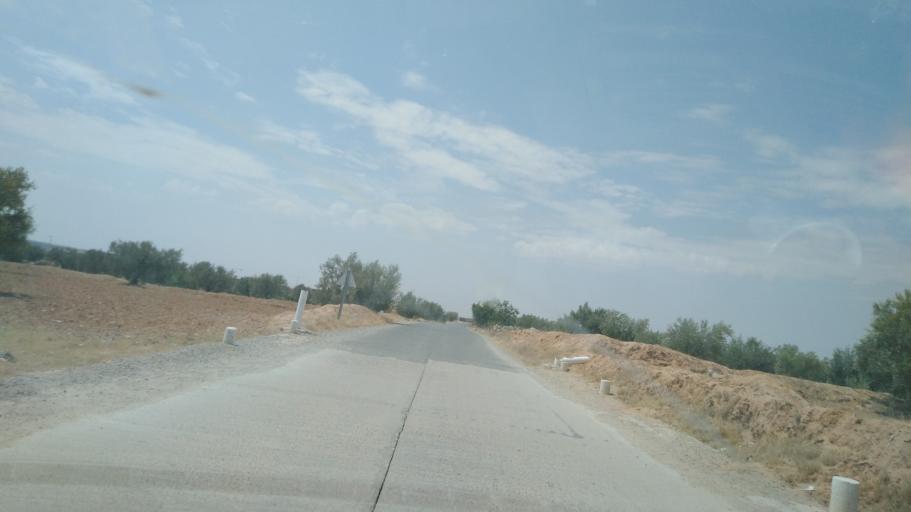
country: TN
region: Safaqis
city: Sfax
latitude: 34.7457
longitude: 10.5541
